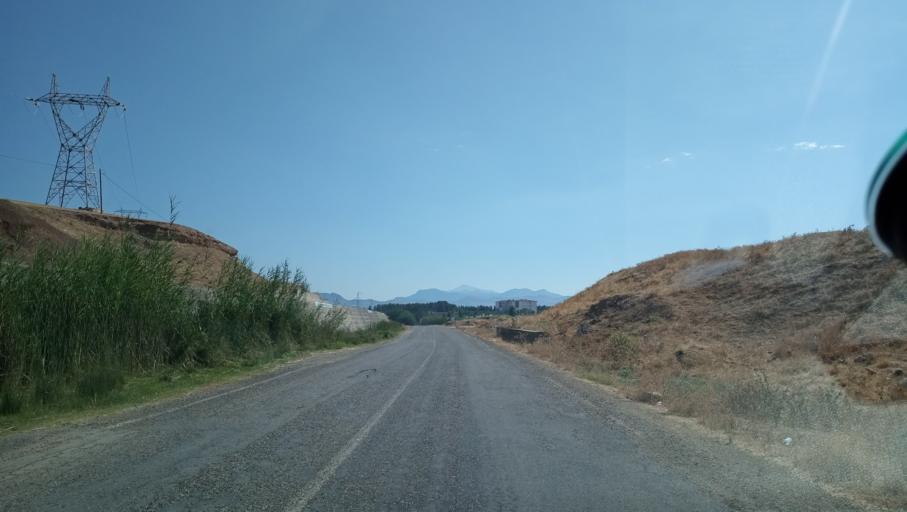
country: TR
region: Diyarbakir
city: Malabadi
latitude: 38.1331
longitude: 41.1870
